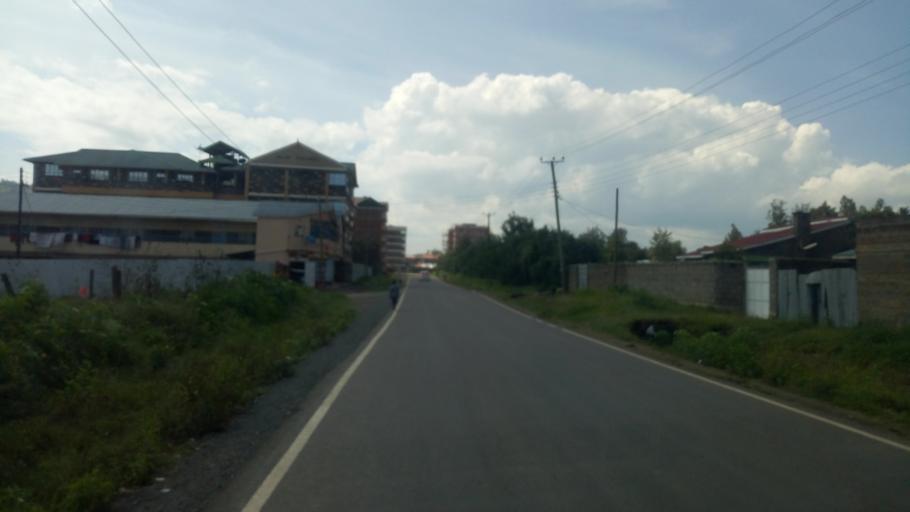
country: KE
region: Nakuru
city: Nakuru
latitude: -0.2801
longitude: 36.1018
